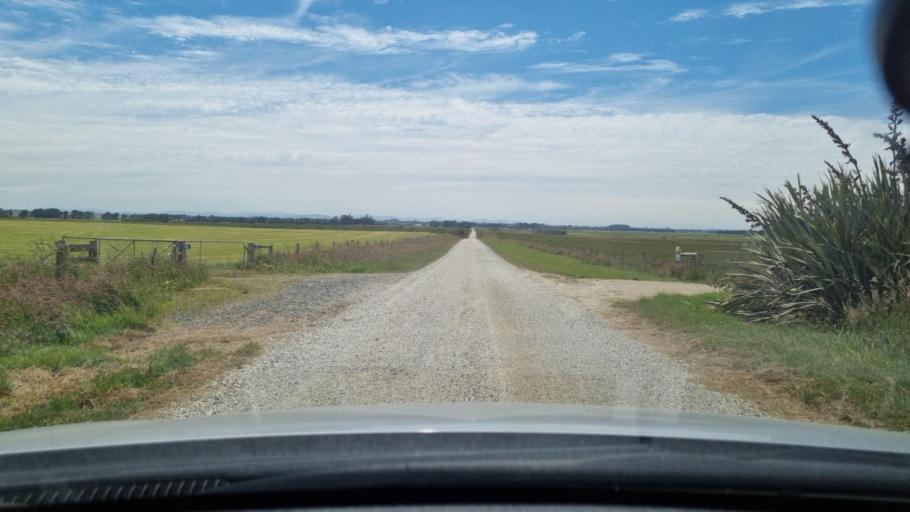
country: NZ
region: Southland
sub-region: Invercargill City
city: Invercargill
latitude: -46.3997
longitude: 168.2630
